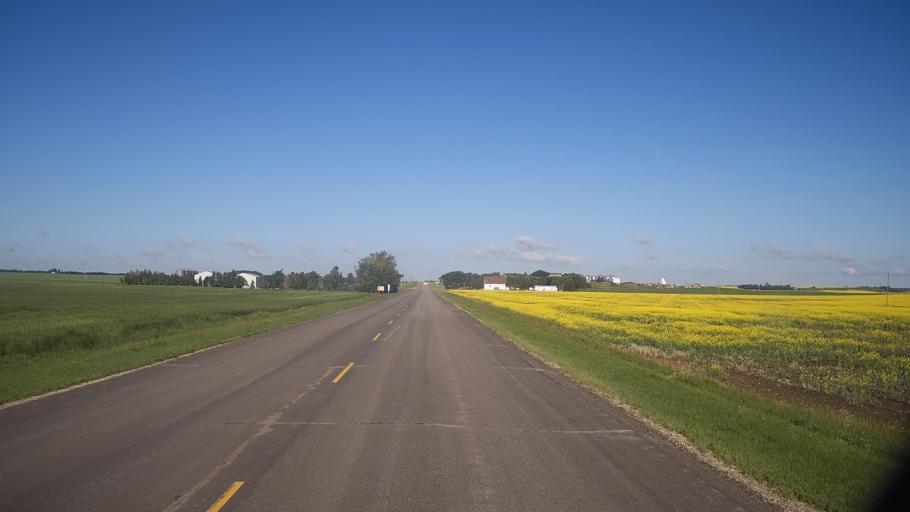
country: CA
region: Saskatchewan
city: Watrous
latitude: 51.6781
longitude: -105.3963
